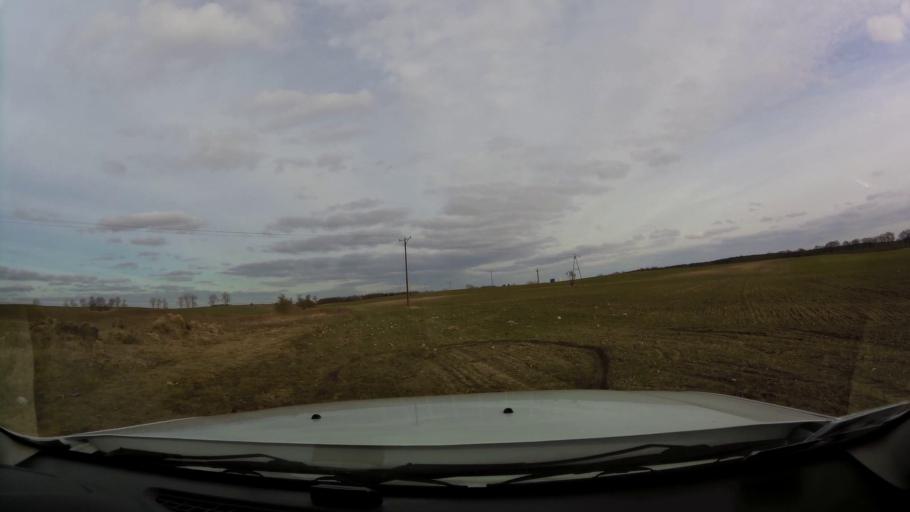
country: PL
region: West Pomeranian Voivodeship
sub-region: Powiat drawski
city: Drawsko Pomorskie
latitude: 53.5184
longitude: 15.7589
